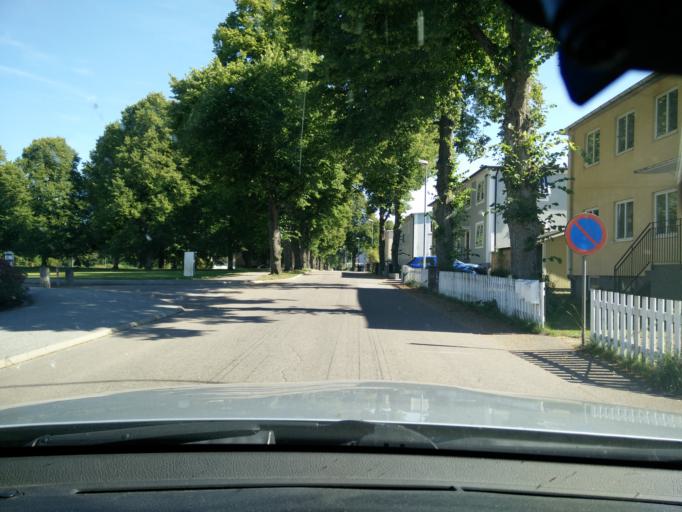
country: SE
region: OEstergoetland
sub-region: Linkopings Kommun
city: Ljungsbro
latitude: 58.5124
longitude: 15.4991
